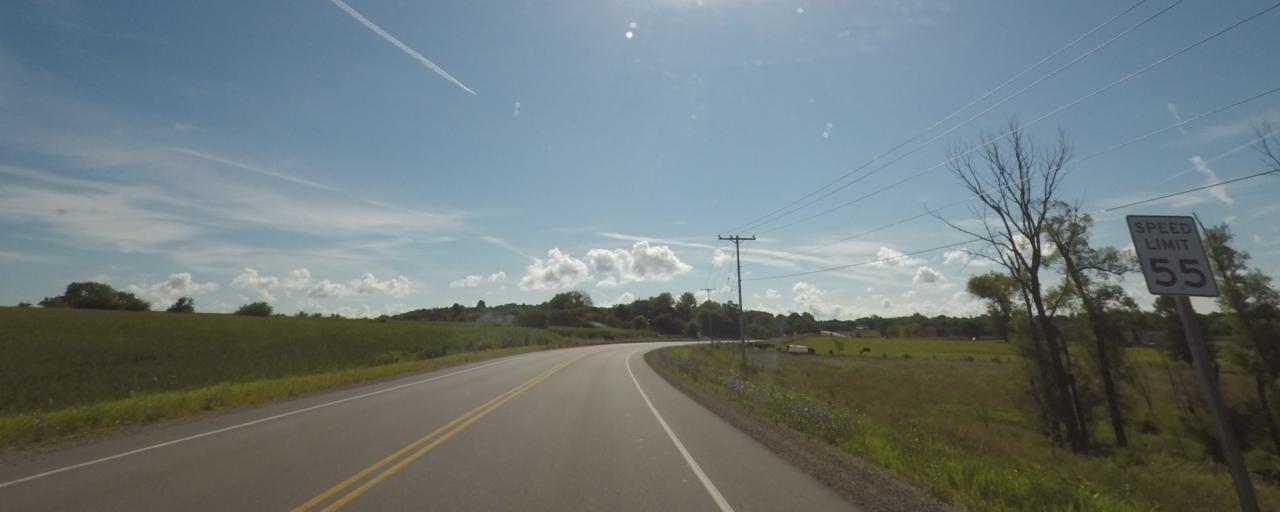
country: US
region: Wisconsin
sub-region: Jefferson County
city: Ixonia
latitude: 43.0760
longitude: -88.6691
